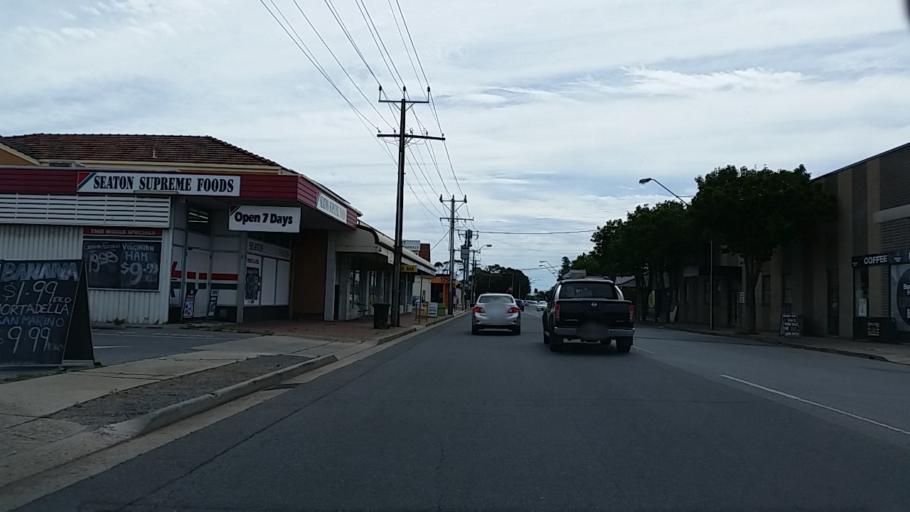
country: AU
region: South Australia
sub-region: Charles Sturt
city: Seaton
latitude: -34.8918
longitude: 138.5160
